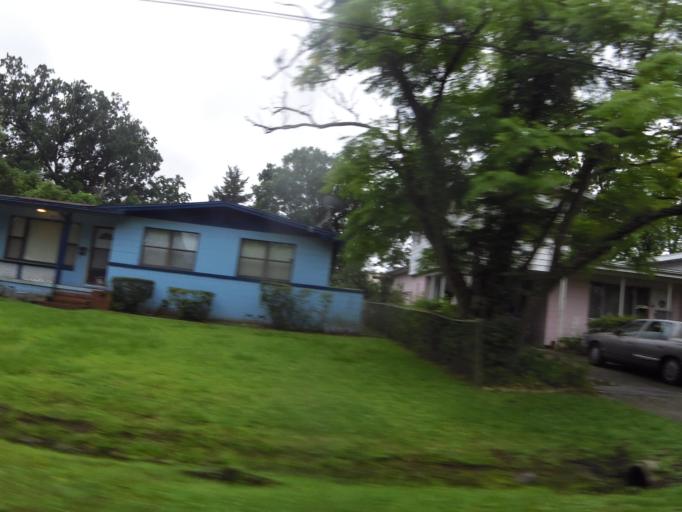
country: US
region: Florida
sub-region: Duval County
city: Jacksonville
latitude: 30.2860
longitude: -81.6301
